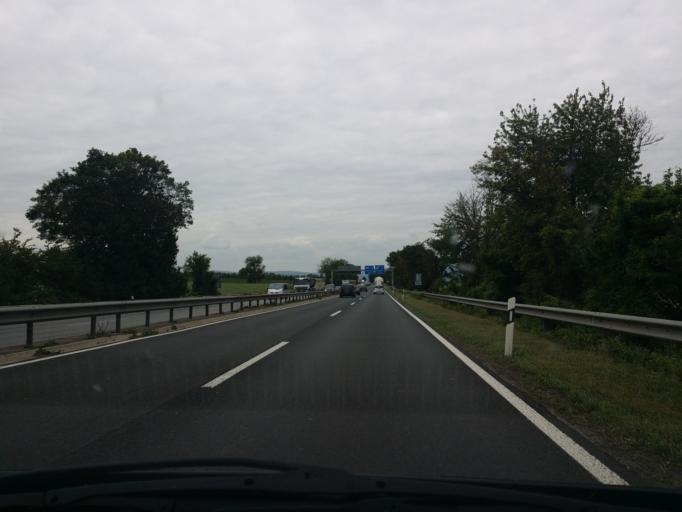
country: DE
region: Rheinland-Pfalz
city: Klein-Winternheim
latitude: 49.9752
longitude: 8.2137
